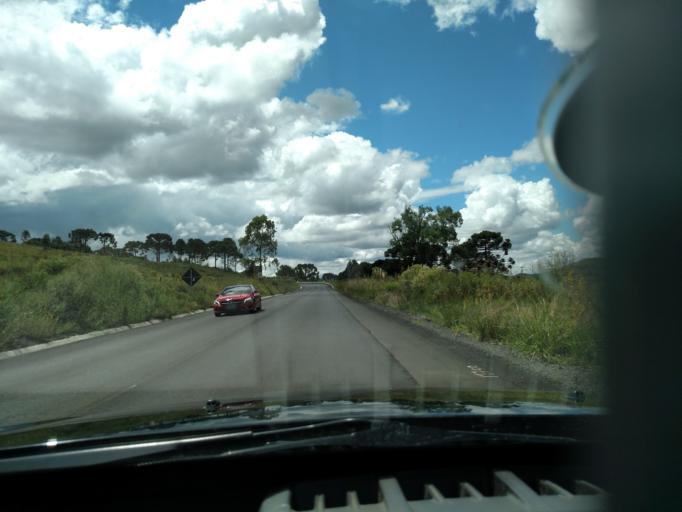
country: BR
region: Santa Catarina
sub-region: Sao Joaquim
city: Sao Joaquim
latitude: -28.2002
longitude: -49.9948
